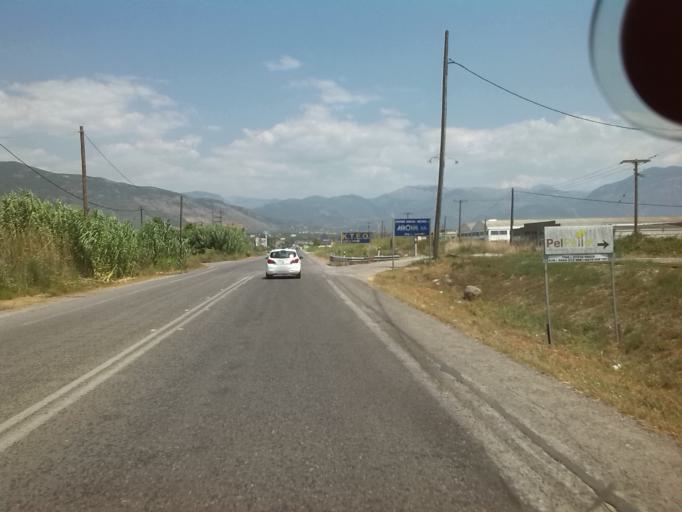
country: GR
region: Peloponnese
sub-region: Nomos Messinias
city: Sperkhoyia
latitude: 37.0561
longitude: 22.0493
